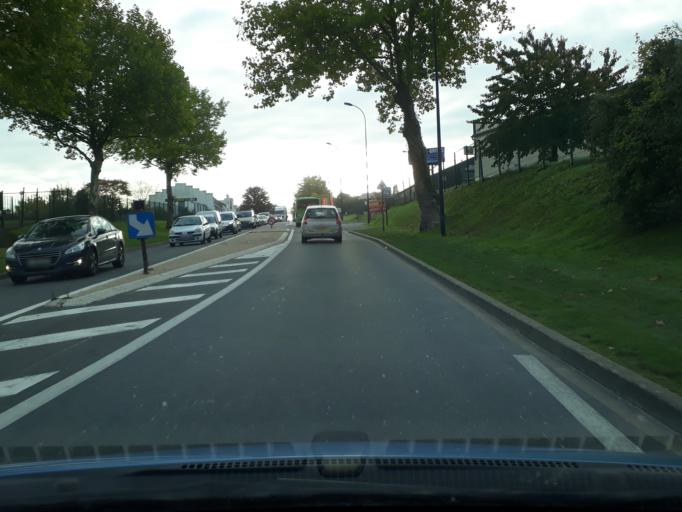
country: FR
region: Ile-de-France
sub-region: Departement de Seine-et-Marne
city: Ecuelles
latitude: 48.3684
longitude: 2.8366
